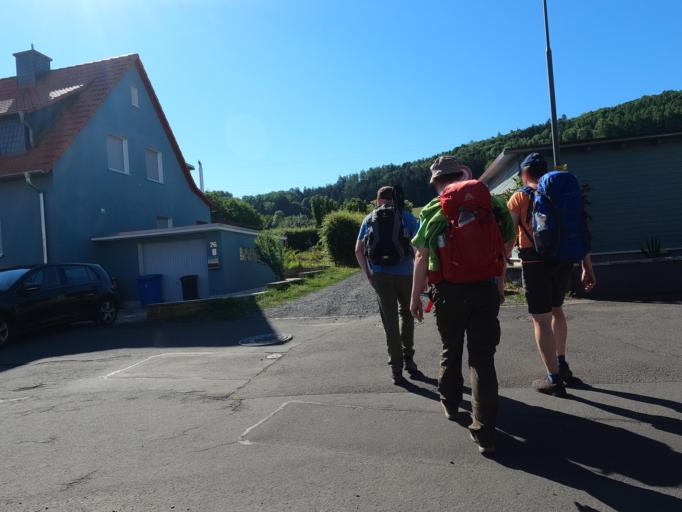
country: DE
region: Hesse
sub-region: Regierungsbezirk Darmstadt
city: Schluchtern
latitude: 50.3436
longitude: 9.5321
